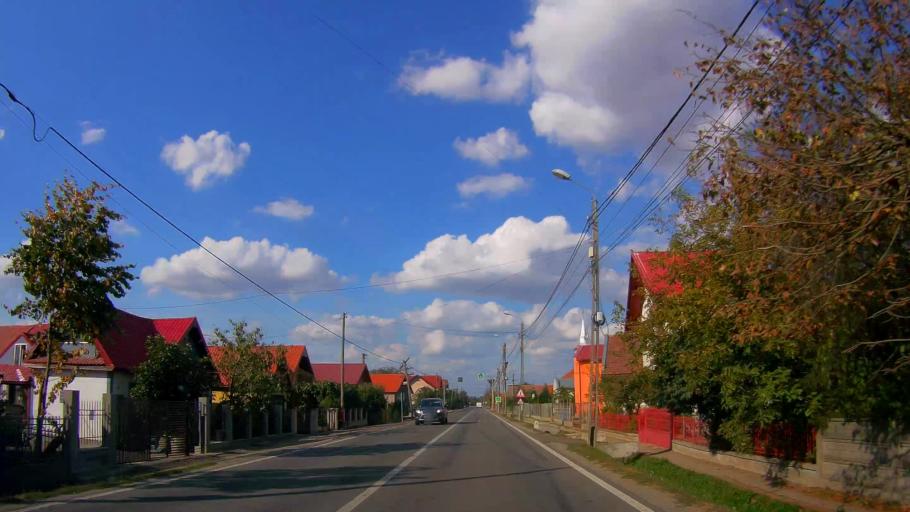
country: RO
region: Satu Mare
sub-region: Comuna Turulung
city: Draguseni
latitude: 47.9049
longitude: 23.0761
